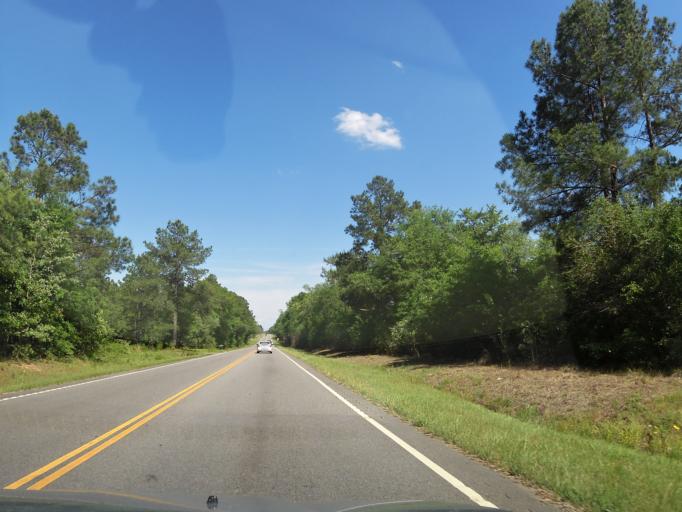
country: US
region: South Carolina
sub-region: Aiken County
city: New Ellenton
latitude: 33.5154
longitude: -81.5814
